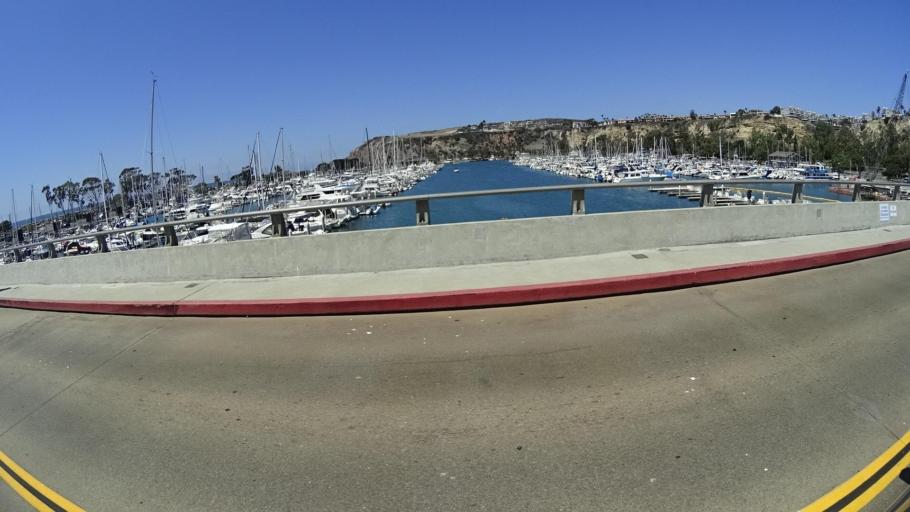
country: US
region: California
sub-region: Orange County
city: Dana Point
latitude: 33.4594
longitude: -117.6986
